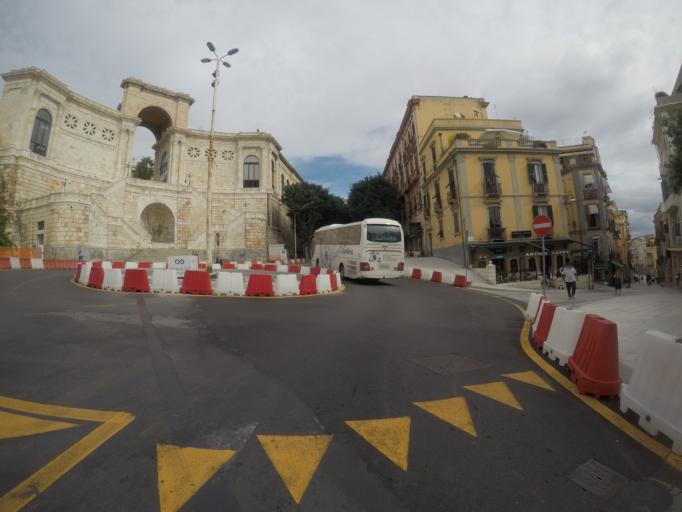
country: IT
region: Sardinia
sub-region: Provincia di Cagliari
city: Cagliari
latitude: 39.2155
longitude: 9.1168
